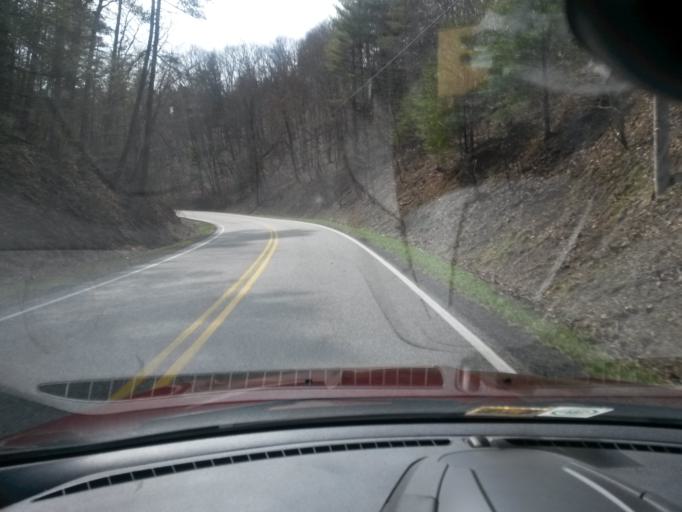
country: US
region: West Virginia
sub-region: Greenbrier County
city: White Sulphur Springs
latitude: 37.6770
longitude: -80.2339
